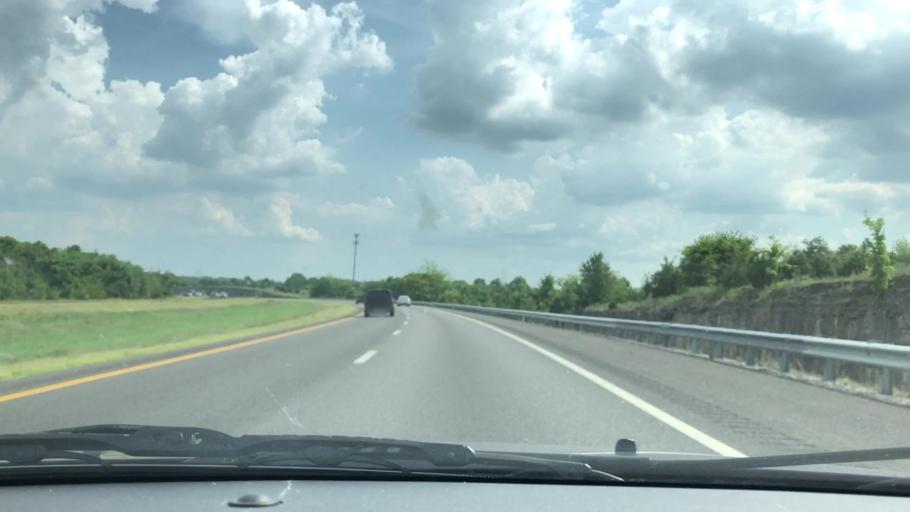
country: US
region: Tennessee
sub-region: Rutherford County
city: Smyrna
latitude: 35.9699
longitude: -86.4489
